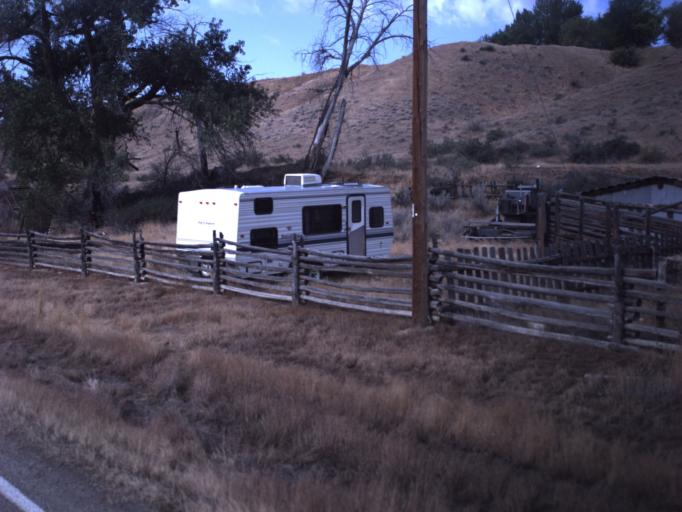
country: US
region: Utah
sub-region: Uintah County
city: Naples
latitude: 40.4152
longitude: -109.3398
